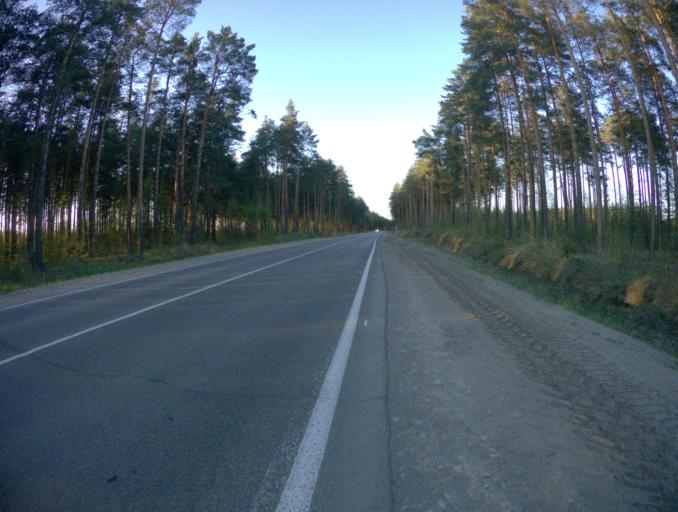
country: RU
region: Vladimir
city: Golovino
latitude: 56.0317
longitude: 40.4121
